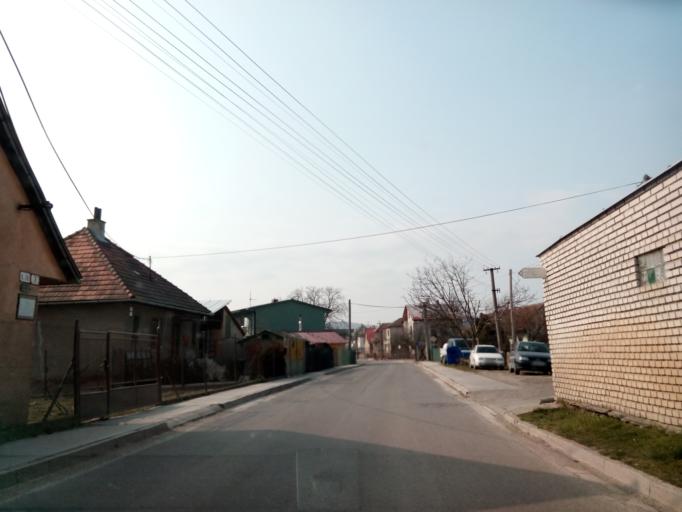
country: SK
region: Trenciansky
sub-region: Okres Trencin
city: Trencin
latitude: 48.9033
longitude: 18.0303
